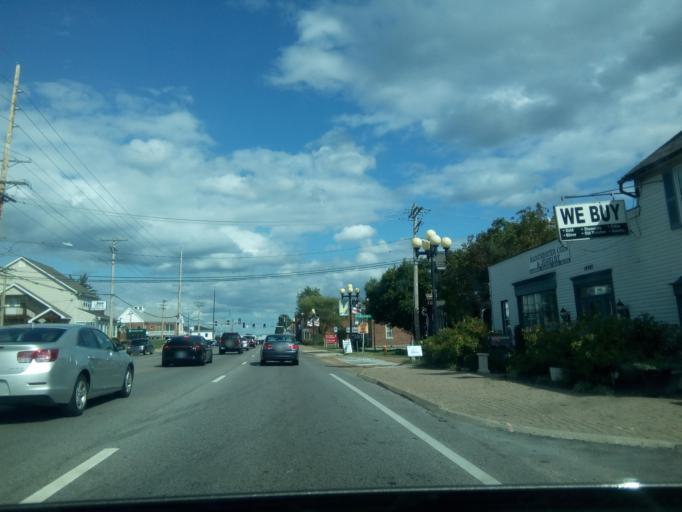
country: US
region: Missouri
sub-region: Saint Louis County
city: Manchester
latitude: 38.5929
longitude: -90.5136
